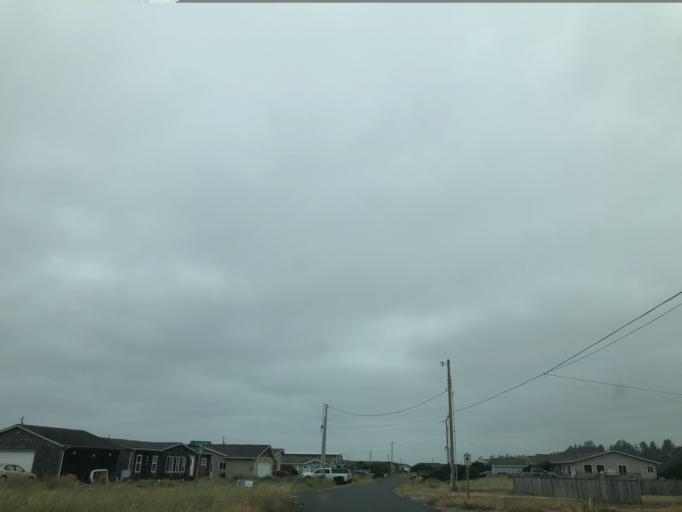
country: US
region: Oregon
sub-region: Lincoln County
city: Waldport
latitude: 44.4279
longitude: -124.0799
